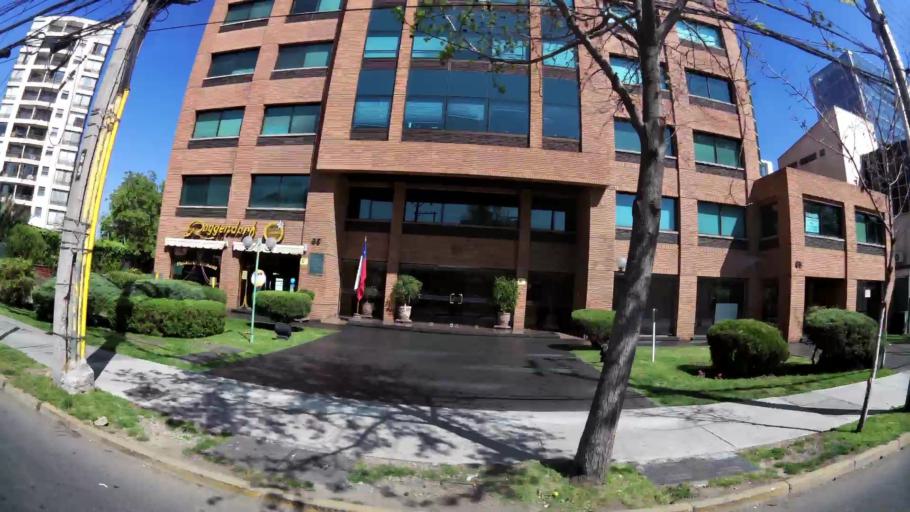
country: CL
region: Santiago Metropolitan
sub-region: Provincia de Santiago
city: Villa Presidente Frei, Nunoa, Santiago, Chile
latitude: -33.4103
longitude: -70.5703
